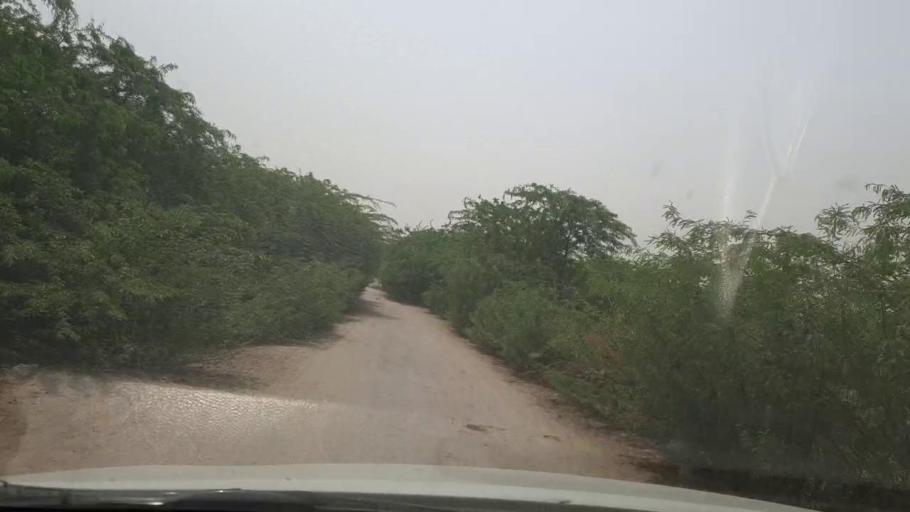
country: PK
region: Sindh
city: Kot Diji
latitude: 27.3433
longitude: 68.7141
